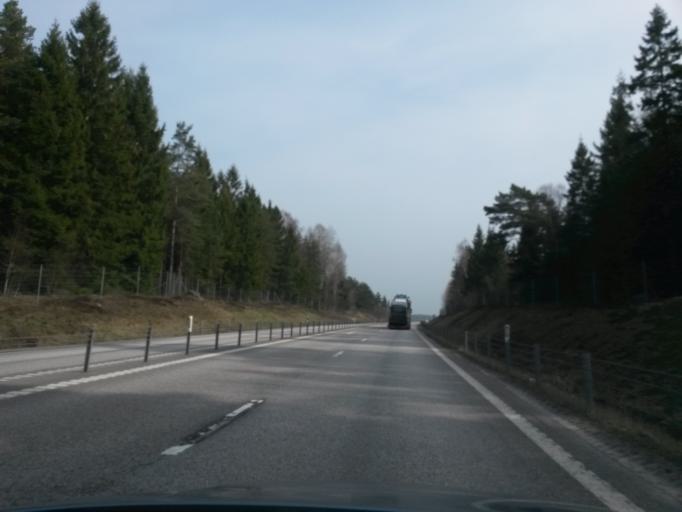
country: SE
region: Vaestra Goetaland
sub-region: Gullspangs Kommun
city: Hova
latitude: 58.8189
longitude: 14.1419
